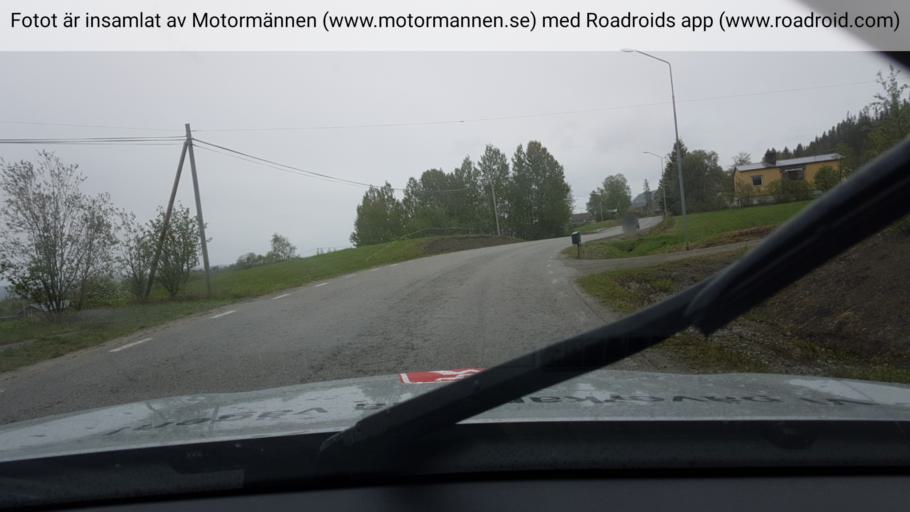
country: SE
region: Jaemtland
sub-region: Bergs Kommun
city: Hoverberg
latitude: 62.7704
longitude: 14.5369
